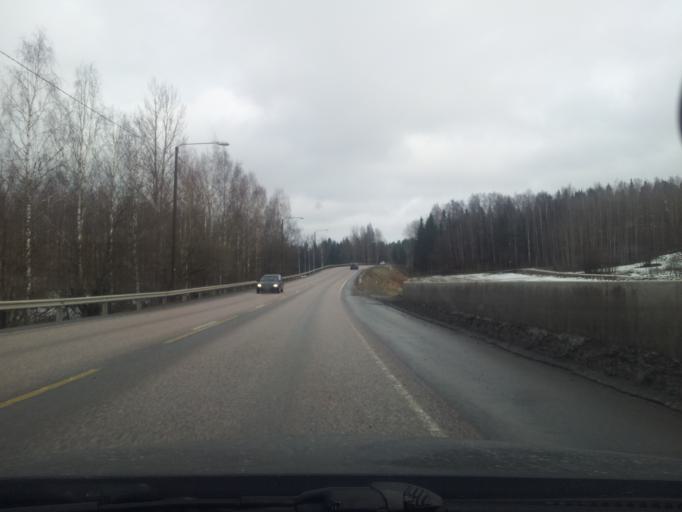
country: FI
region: Uusimaa
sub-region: Helsinki
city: Espoo
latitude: 60.1961
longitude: 24.5841
